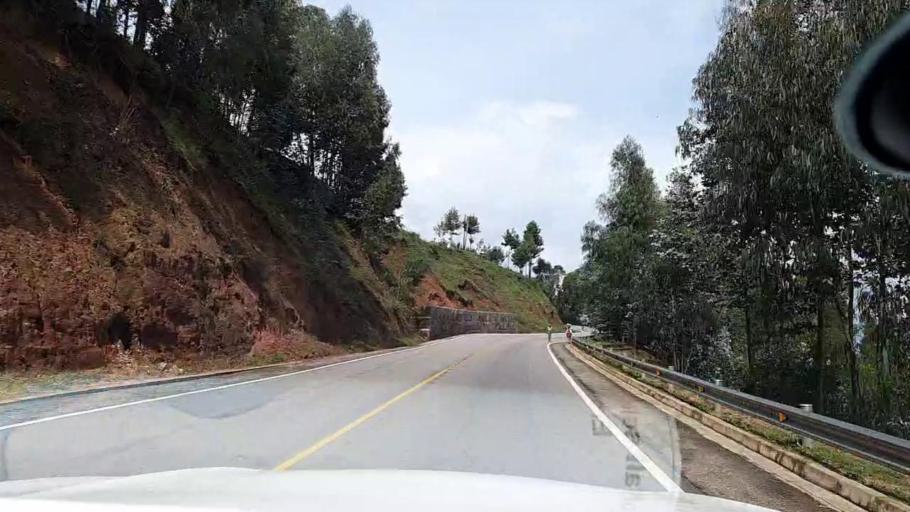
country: RW
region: Southern Province
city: Nzega
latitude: -2.4931
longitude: 29.5085
